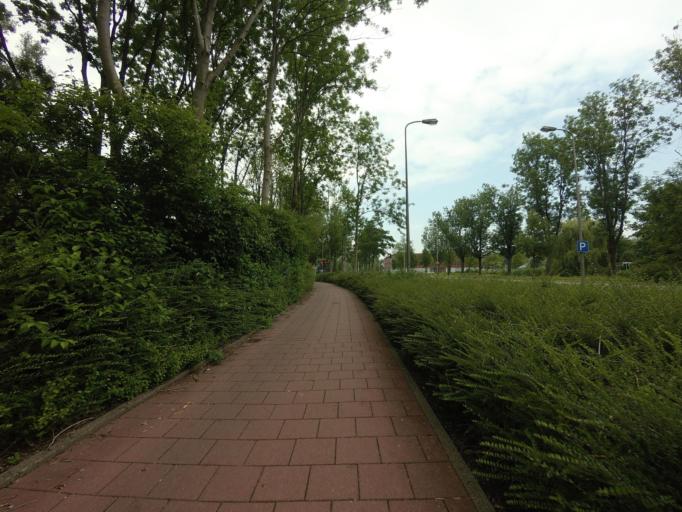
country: NL
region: North Holland
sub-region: Gemeente Purmerend
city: Purmerend
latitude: 52.5183
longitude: 4.9636
